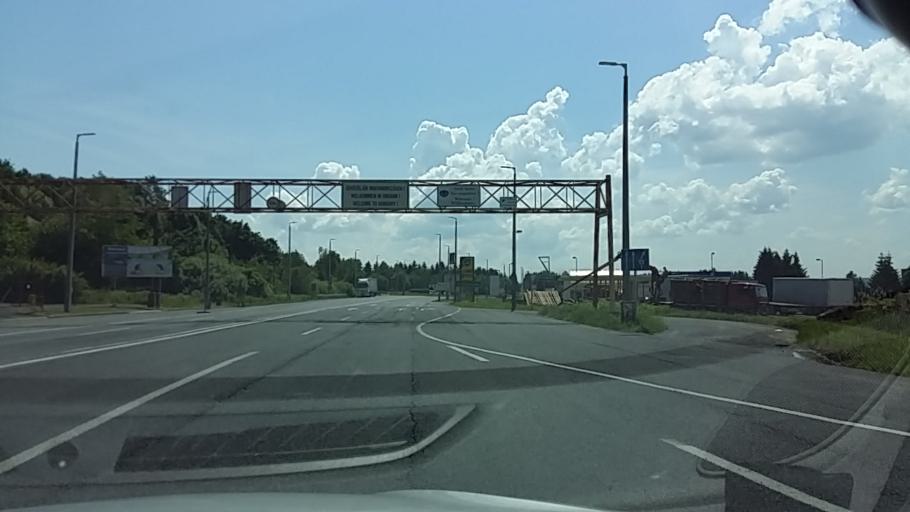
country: AT
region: Burgenland
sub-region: Politischer Bezirk Jennersdorf
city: Heiligenkreuz im Lafnitztal
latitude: 46.9835
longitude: 16.2790
